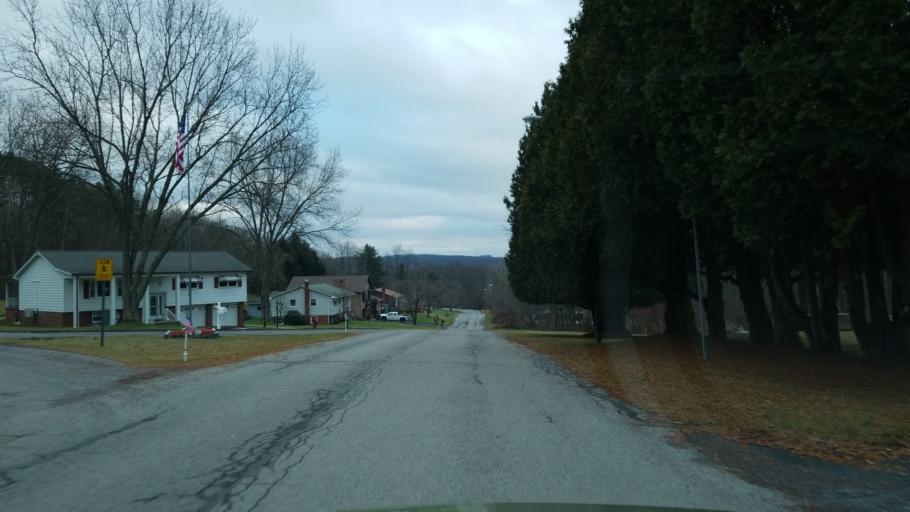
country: US
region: Pennsylvania
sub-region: Jefferson County
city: Falls Creek
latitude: 41.1411
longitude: -78.8106
